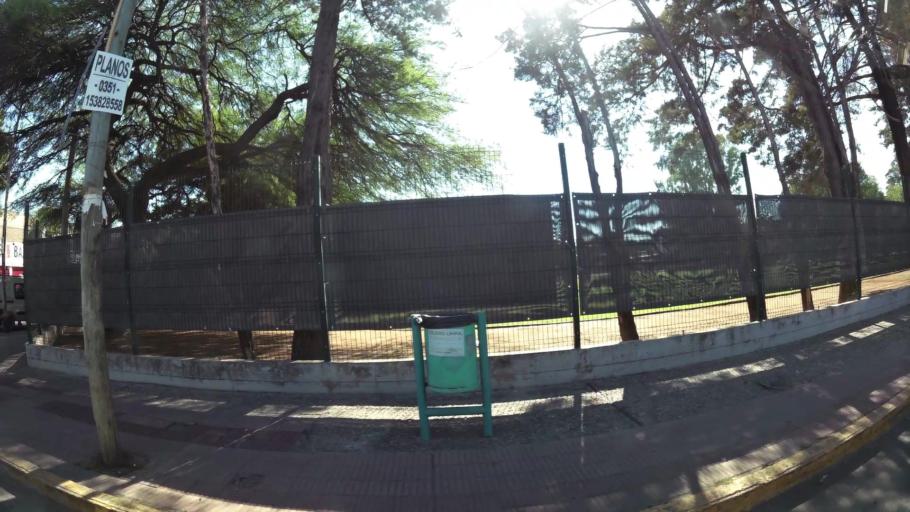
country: AR
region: Cordoba
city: Villa Allende
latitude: -31.3521
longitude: -64.2489
